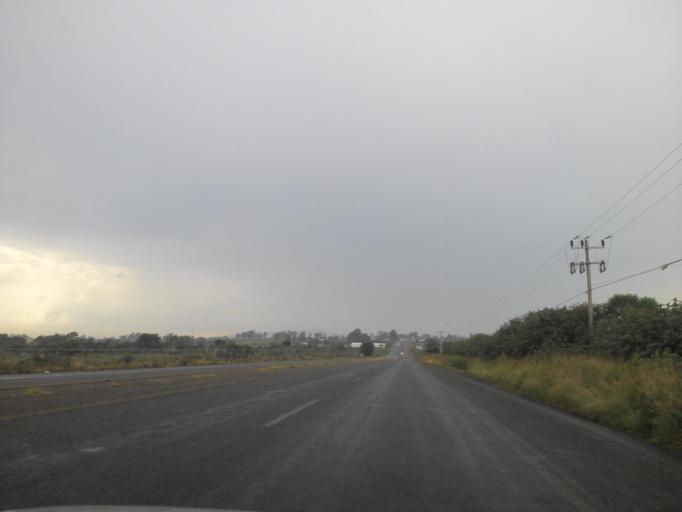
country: MX
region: Jalisco
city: Capilla de Guadalupe
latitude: 20.8626
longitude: -102.6377
